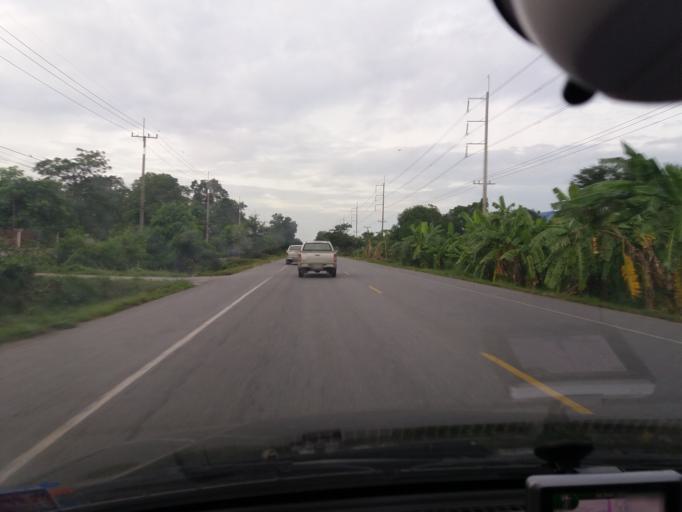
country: TH
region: Suphan Buri
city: U Thong
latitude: 14.5038
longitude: 99.9179
